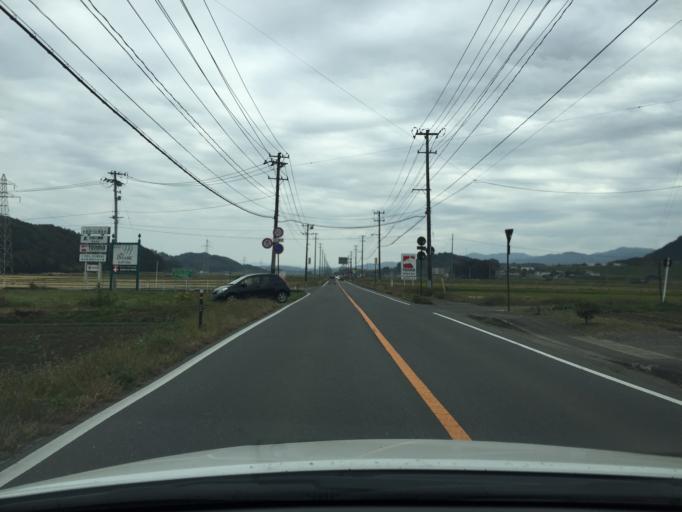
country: JP
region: Fukushima
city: Ishikawa
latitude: 37.0874
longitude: 140.2656
